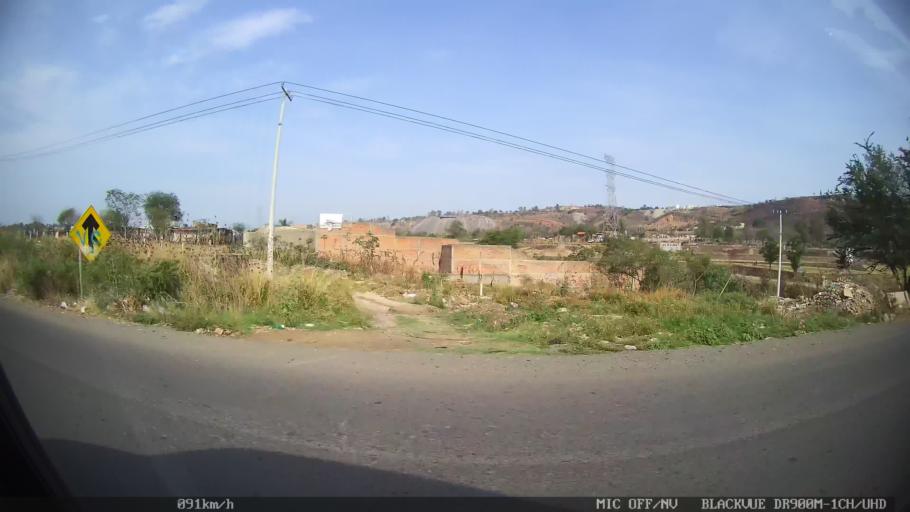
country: MX
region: Jalisco
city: Coyula
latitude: 20.6297
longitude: -103.2112
